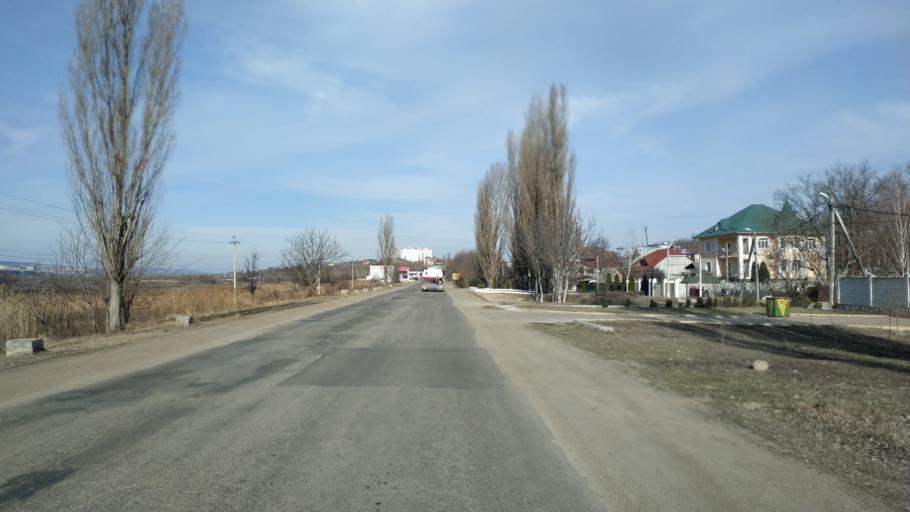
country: MD
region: Laloveni
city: Ialoveni
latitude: 46.9473
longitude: 28.7705
